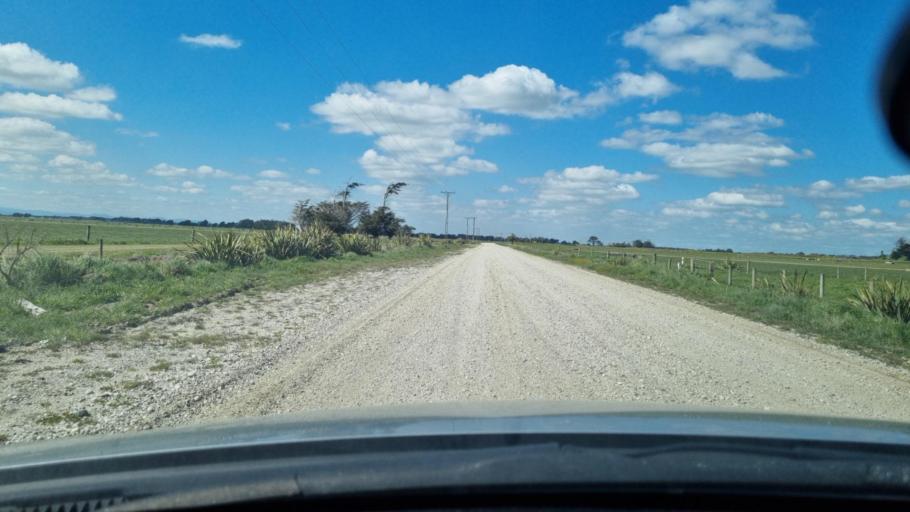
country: NZ
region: Southland
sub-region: Invercargill City
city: Invercargill
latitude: -46.3922
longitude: 168.2514
